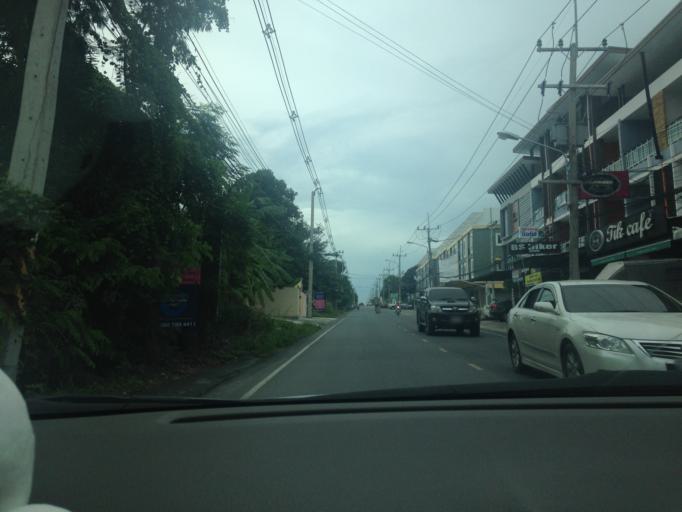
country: TH
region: Chon Buri
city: Chon Buri
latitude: 13.3262
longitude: 100.9272
